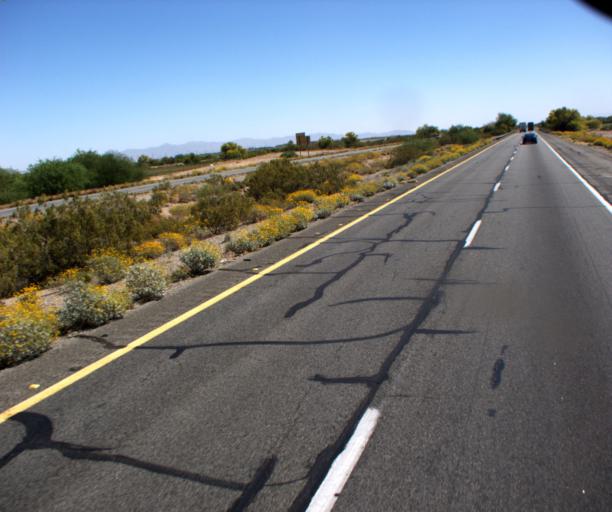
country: US
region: Arizona
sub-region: Maricopa County
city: Buckeye
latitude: 33.4890
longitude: -112.9003
